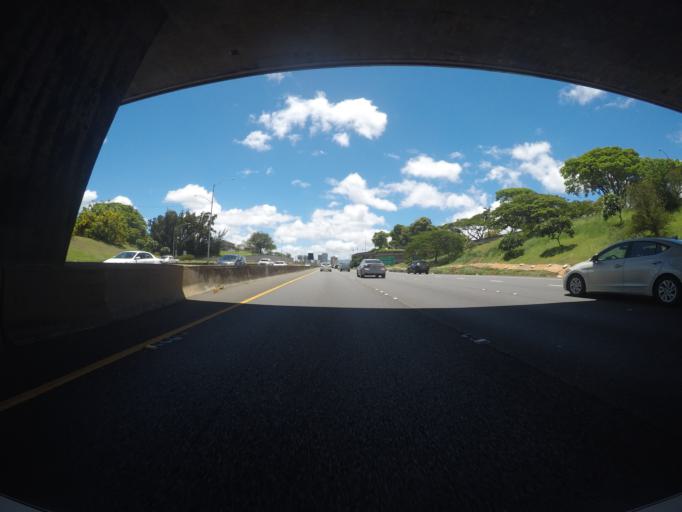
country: US
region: Hawaii
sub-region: Honolulu County
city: Halawa Heights
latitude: 21.3427
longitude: -157.8883
